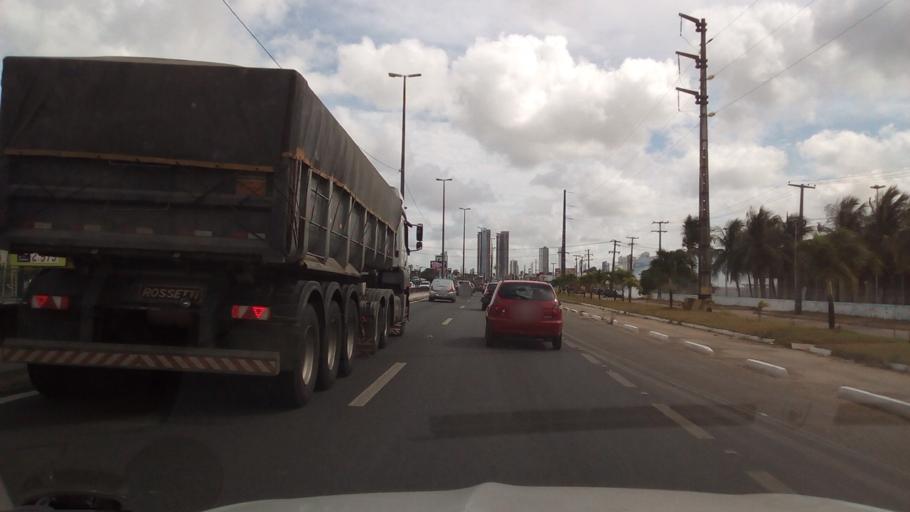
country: BR
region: Paraiba
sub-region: Joao Pessoa
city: Joao Pessoa
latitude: -7.0861
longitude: -34.8487
